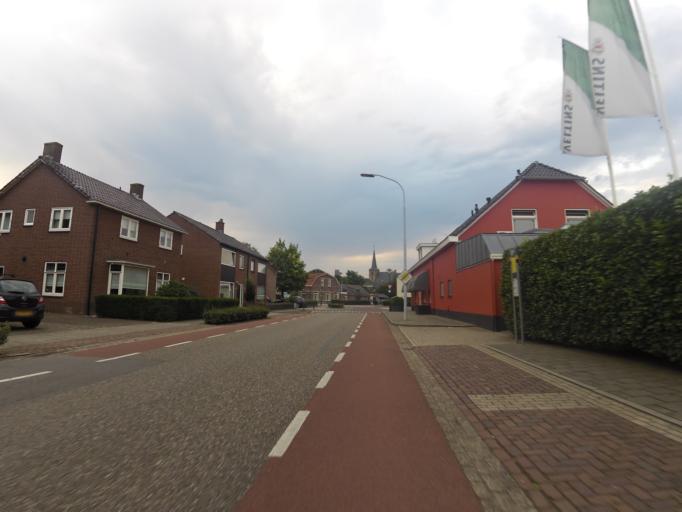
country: NL
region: Gelderland
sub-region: Oude IJsselstreek
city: Gendringen
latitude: 51.9150
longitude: 6.3431
